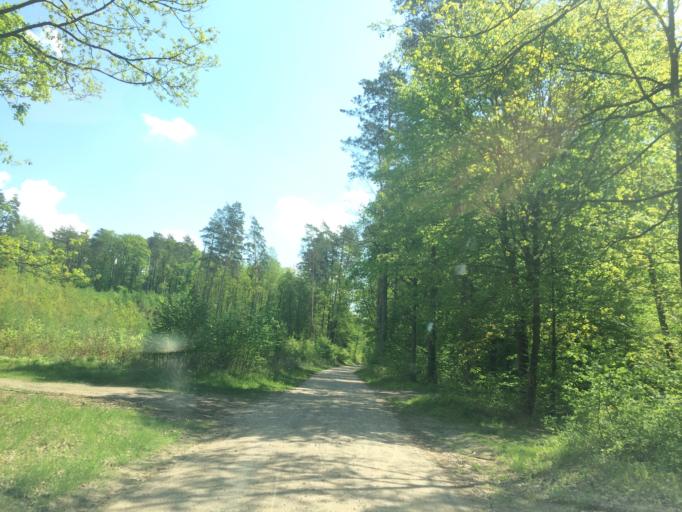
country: PL
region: Warmian-Masurian Voivodeship
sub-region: Powiat nowomiejski
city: Nowe Miasto Lubawskie
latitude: 53.4514
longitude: 19.6180
